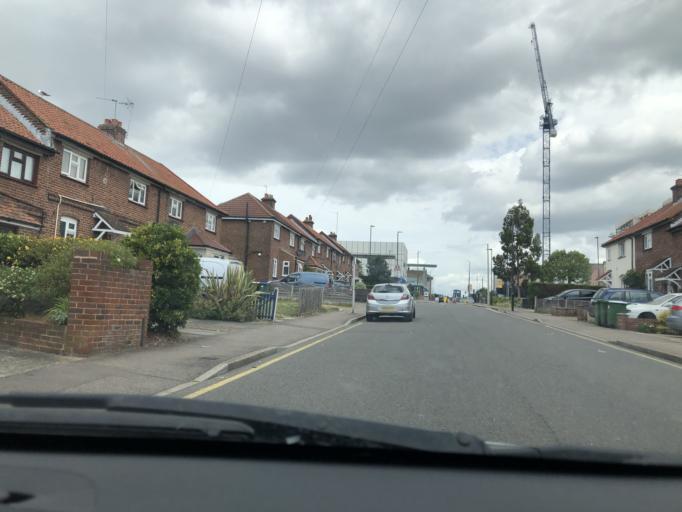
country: GB
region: England
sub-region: Greater London
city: Bexley
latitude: 51.4539
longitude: 0.1486
